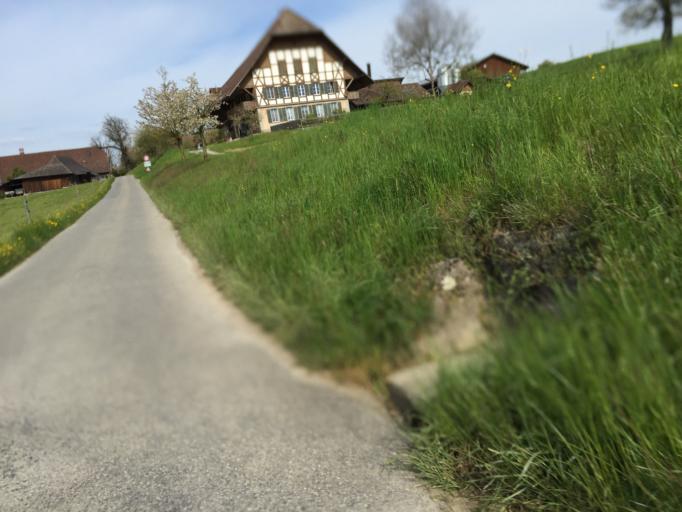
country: CH
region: Bern
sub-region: Bern-Mittelland District
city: Koniz
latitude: 46.9151
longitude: 7.3838
